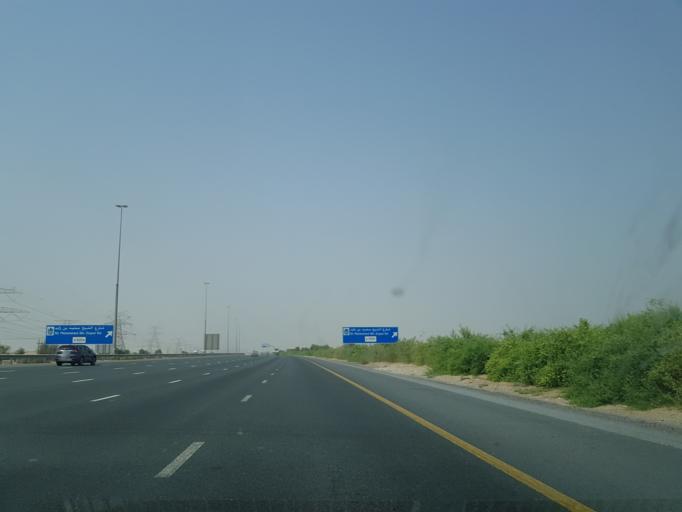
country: AE
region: Dubai
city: Dubai
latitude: 25.0562
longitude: 55.3164
